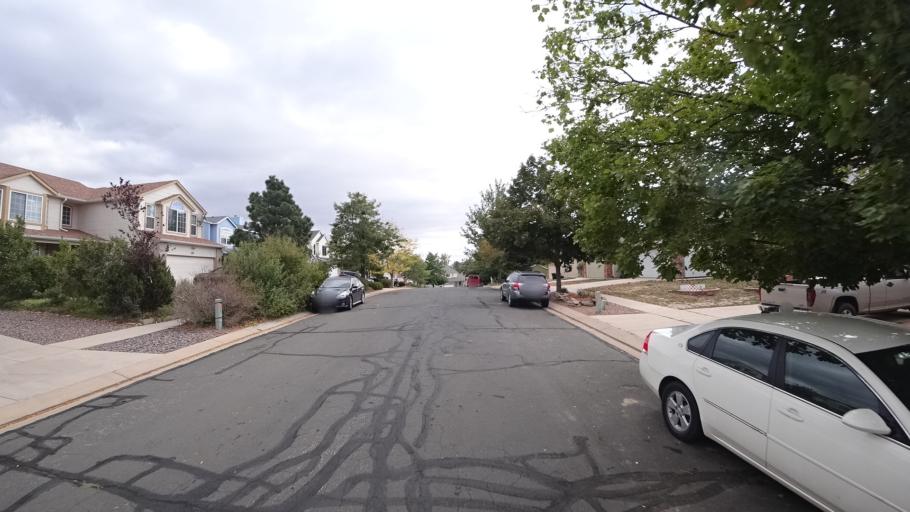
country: US
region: Colorado
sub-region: El Paso County
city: Cimarron Hills
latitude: 38.8857
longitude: -104.7333
